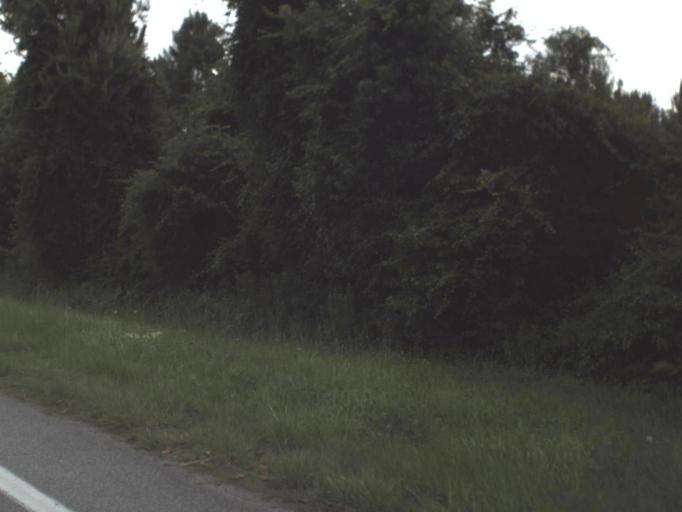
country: US
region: Florida
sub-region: Columbia County
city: Watertown
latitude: 30.1774
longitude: -82.5909
